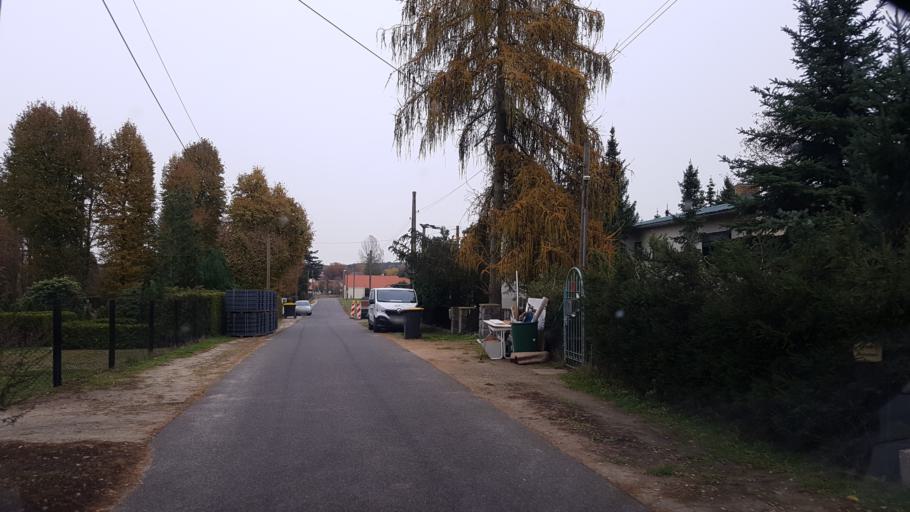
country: DE
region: Brandenburg
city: Crinitz
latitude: 51.7393
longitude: 13.7552
